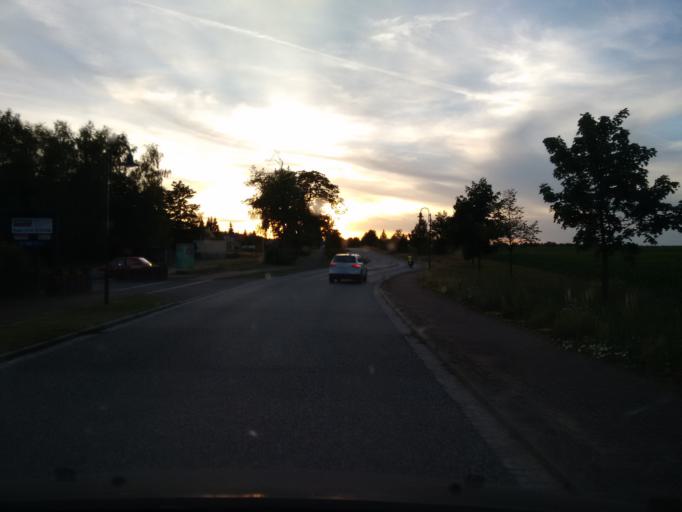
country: DE
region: Brandenburg
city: Mixdorf
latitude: 52.1606
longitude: 14.3862
